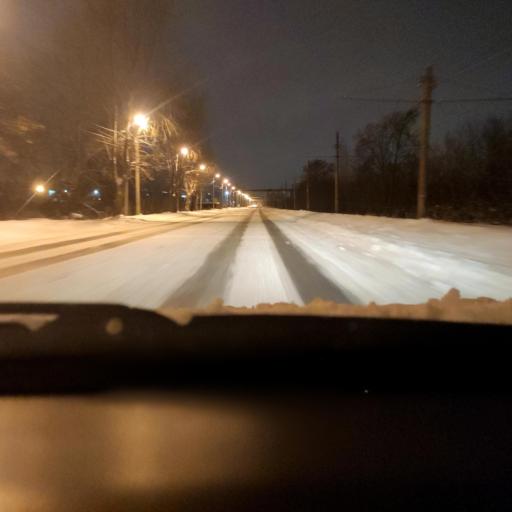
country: RU
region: Perm
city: Kondratovo
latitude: 57.9393
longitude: 56.1235
